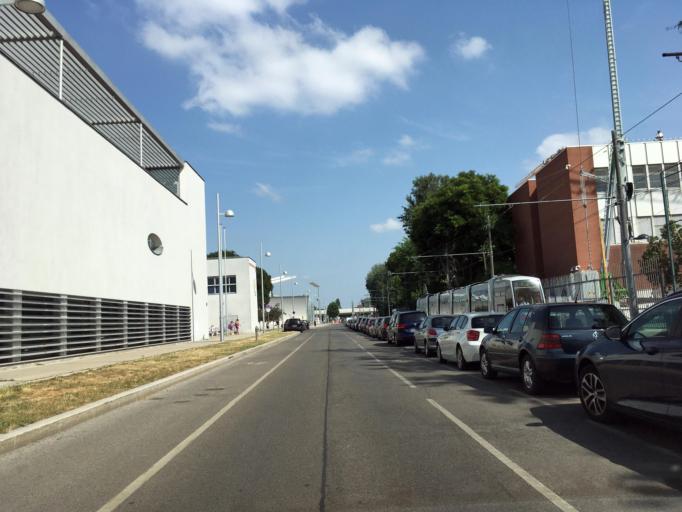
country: AT
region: Lower Austria
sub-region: Politischer Bezirk Wien-Umgebung
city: Gerasdorf bei Wien
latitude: 48.2463
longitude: 16.4306
